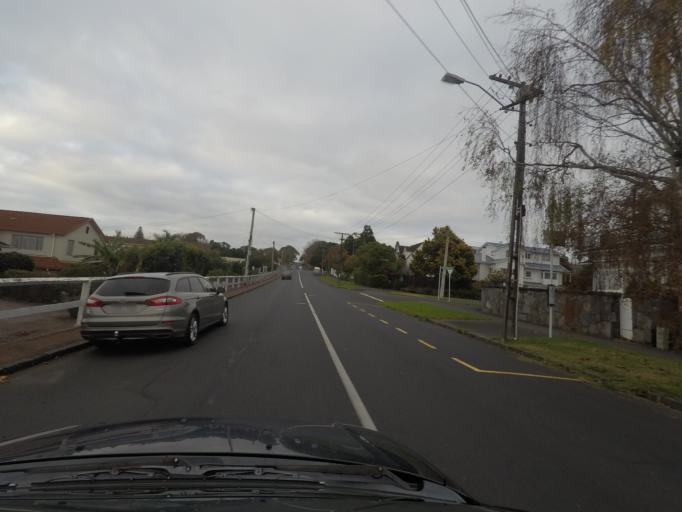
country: NZ
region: Auckland
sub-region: Auckland
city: Auckland
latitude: -36.8898
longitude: 174.7665
